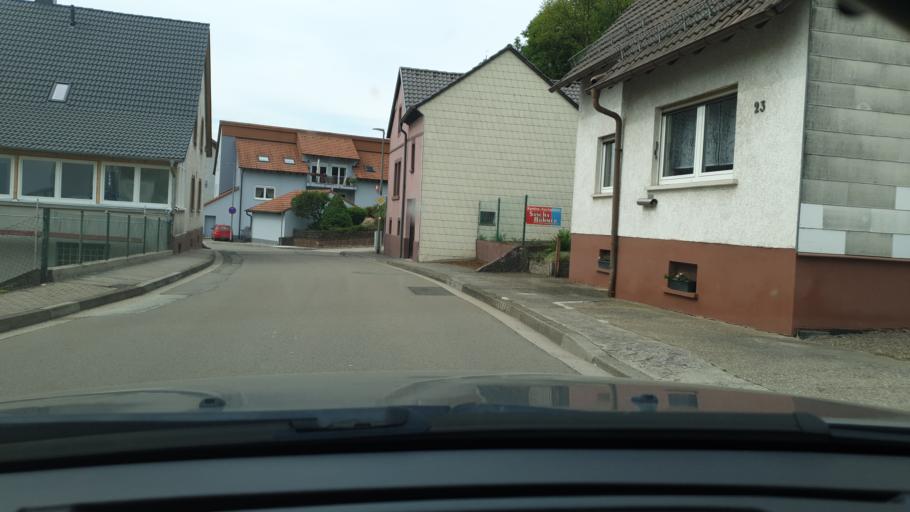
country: DE
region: Rheinland-Pfalz
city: Hauptstuhl
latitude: 49.3899
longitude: 7.4677
